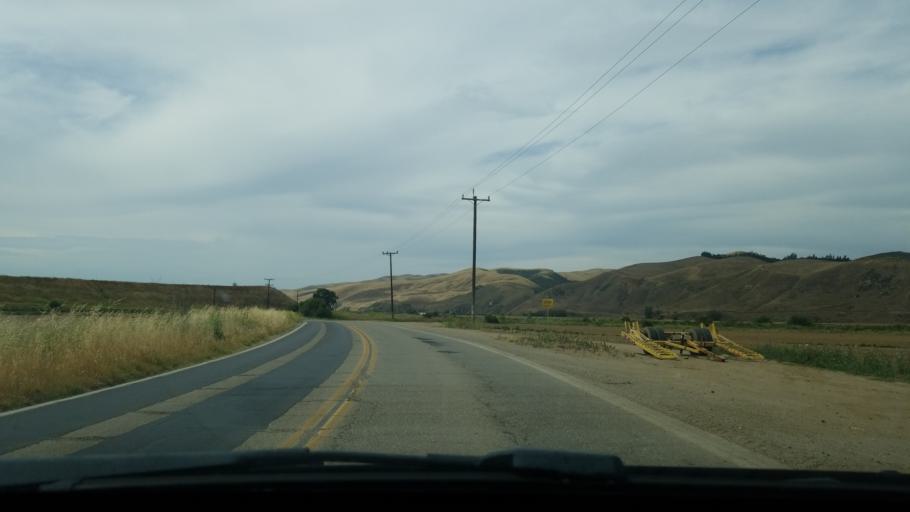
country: US
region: California
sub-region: Santa Barbara County
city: Orcutt
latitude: 34.8996
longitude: -120.3155
